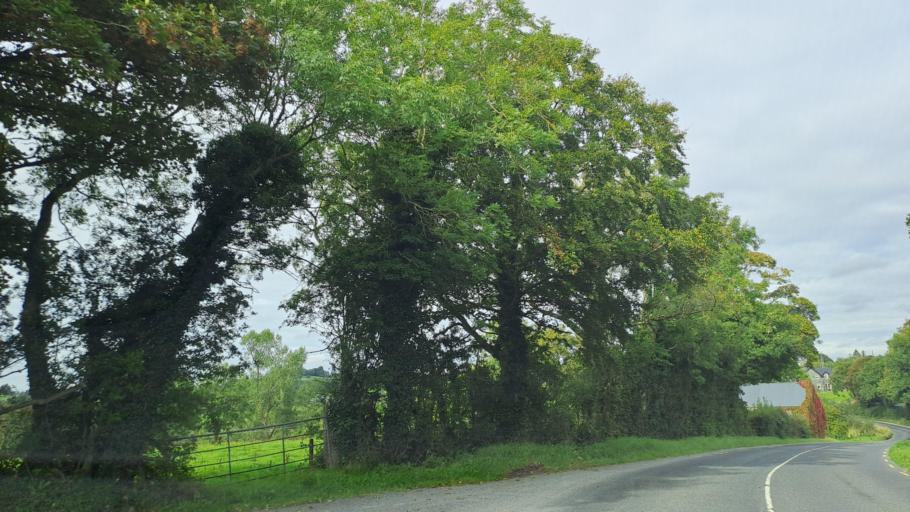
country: IE
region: Ulster
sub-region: An Cabhan
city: Bailieborough
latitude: 53.9892
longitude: -6.8866
